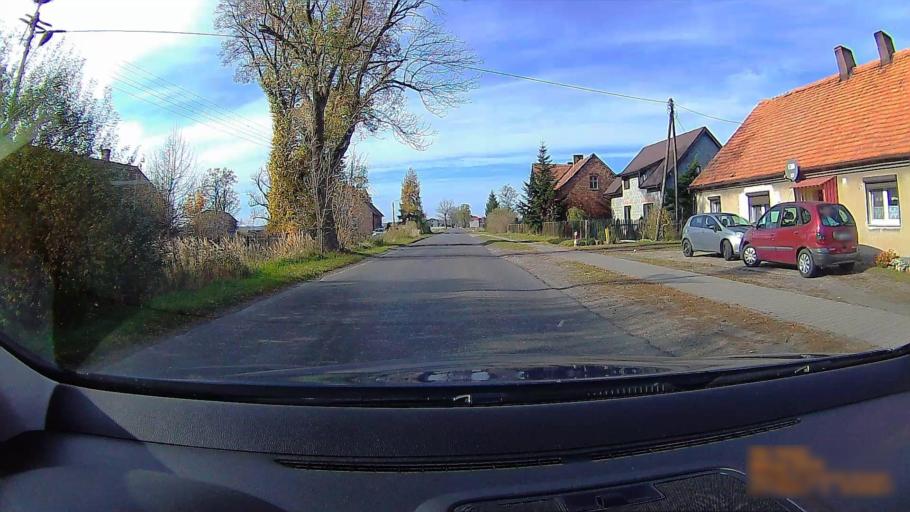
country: PL
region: Greater Poland Voivodeship
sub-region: Powiat ostrzeszowski
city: Doruchow
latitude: 51.4285
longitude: 18.0462
